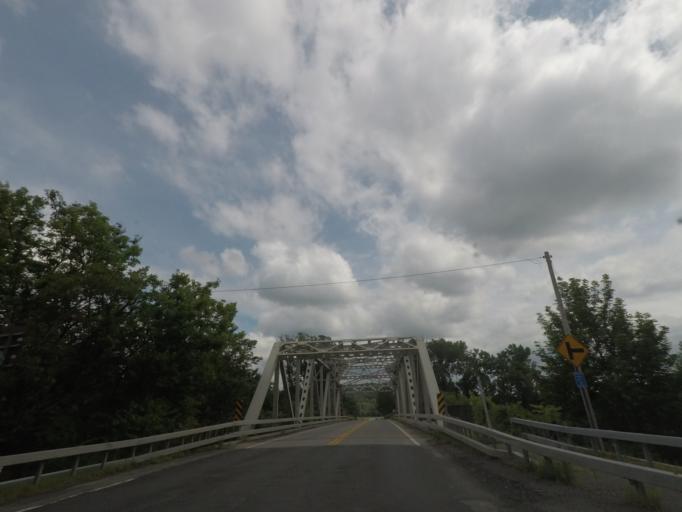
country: US
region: New York
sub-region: Saratoga County
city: Stillwater
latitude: 42.9373
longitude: -73.6499
